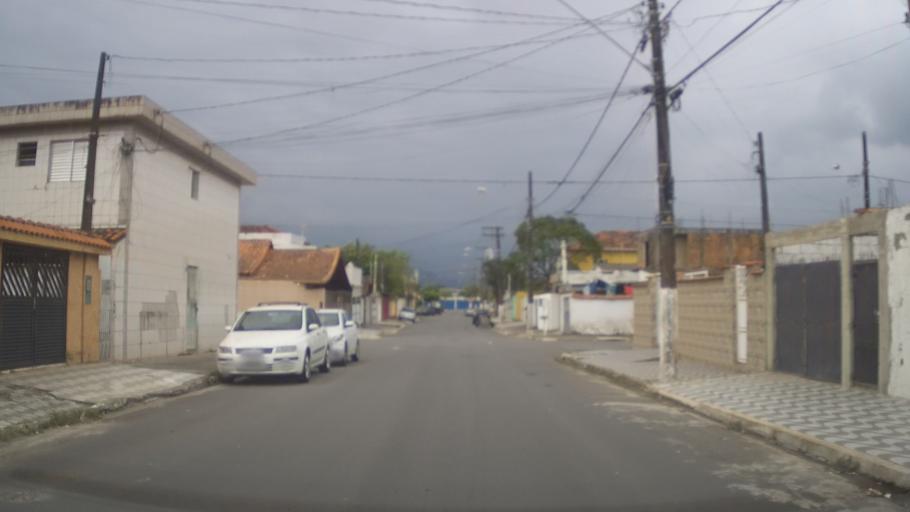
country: BR
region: Sao Paulo
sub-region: Praia Grande
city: Praia Grande
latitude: -24.0058
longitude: -46.4479
